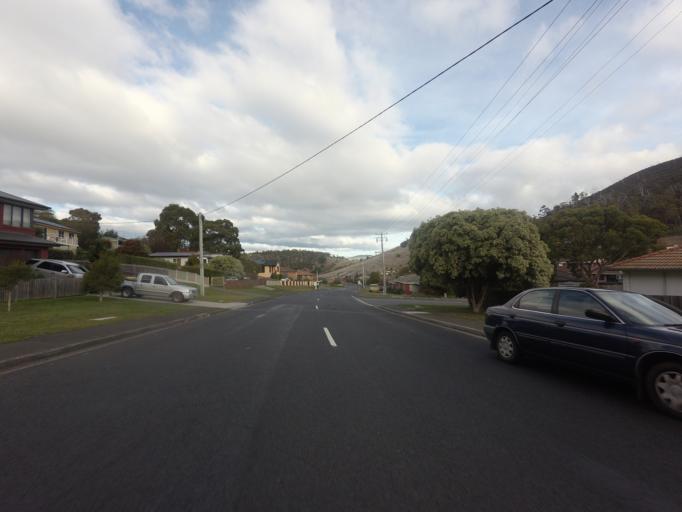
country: AU
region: Tasmania
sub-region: Glenorchy
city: Berriedale
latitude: -42.8207
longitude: 147.2460
